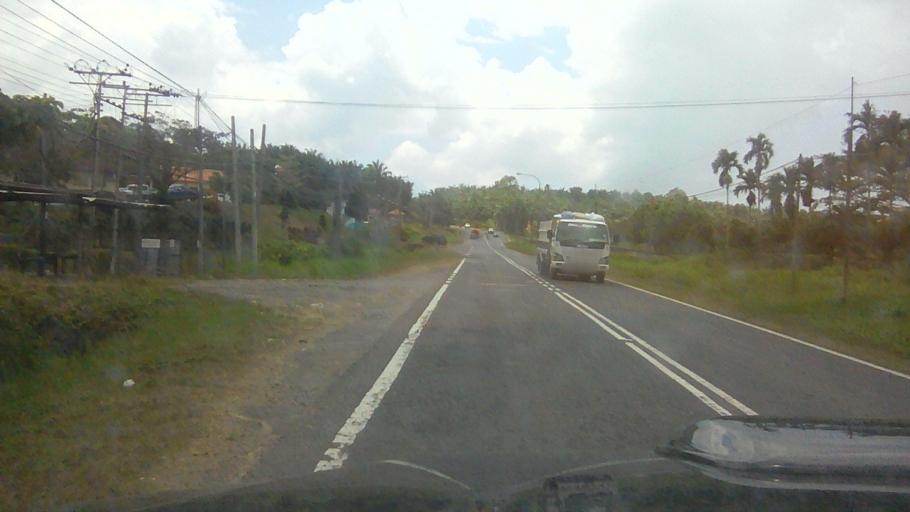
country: MY
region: Sabah
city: Lahad Datu
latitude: 5.0310
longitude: 118.4153
